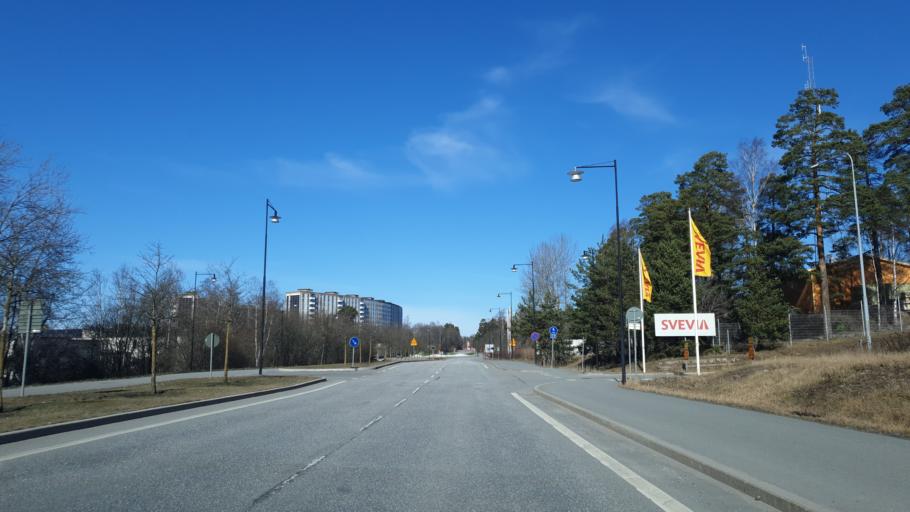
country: SE
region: Stockholm
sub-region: Jarfalla Kommun
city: Jakobsberg
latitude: 59.4232
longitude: 17.8486
